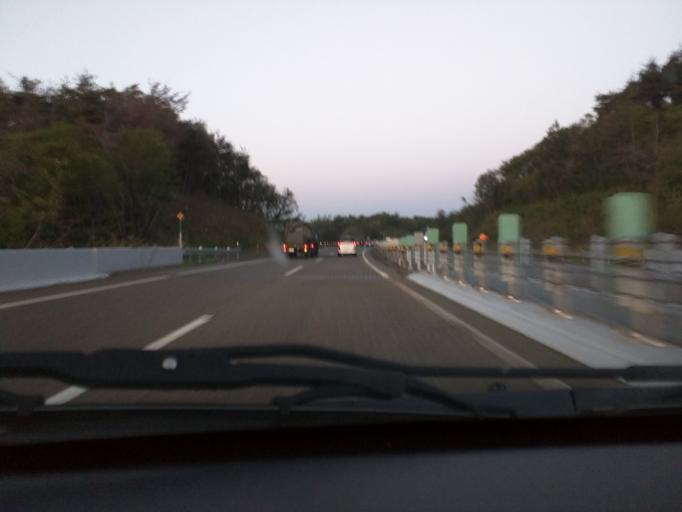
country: JP
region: Niigata
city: Kashiwazaki
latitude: 37.3486
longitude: 138.5021
